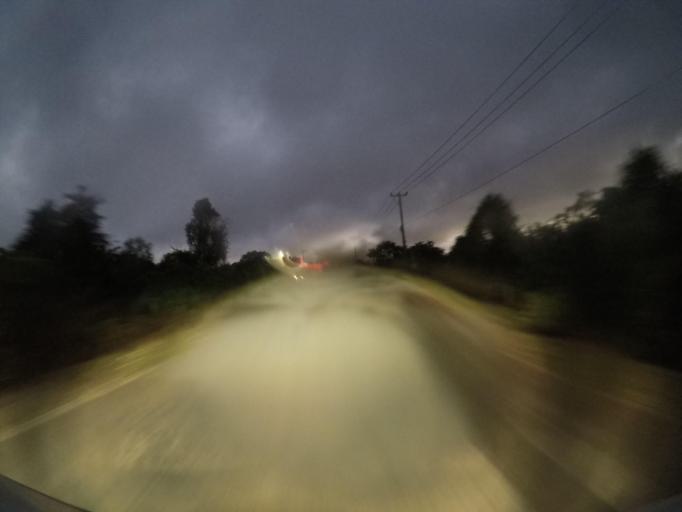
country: TL
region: Lautem
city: Lospalos
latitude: -8.4243
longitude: 127.0048
